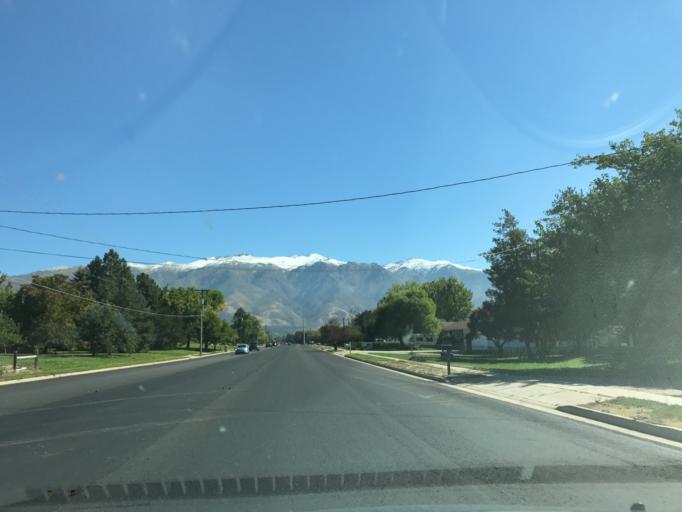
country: US
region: Utah
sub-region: Davis County
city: Hill Air Force Bace
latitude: 41.0891
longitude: -111.9573
